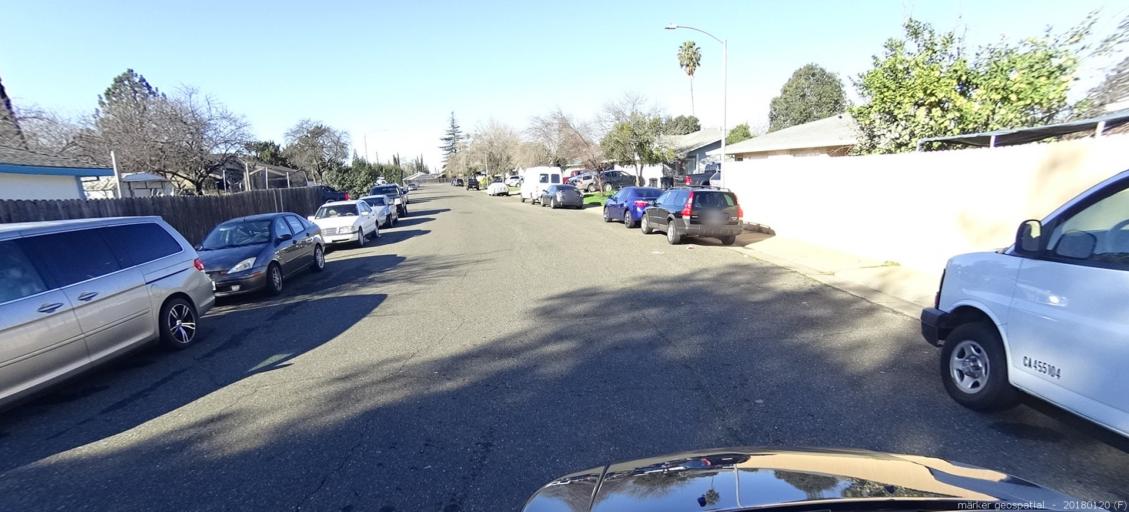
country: US
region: California
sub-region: Sacramento County
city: Rancho Cordova
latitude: 38.5715
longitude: -121.3158
